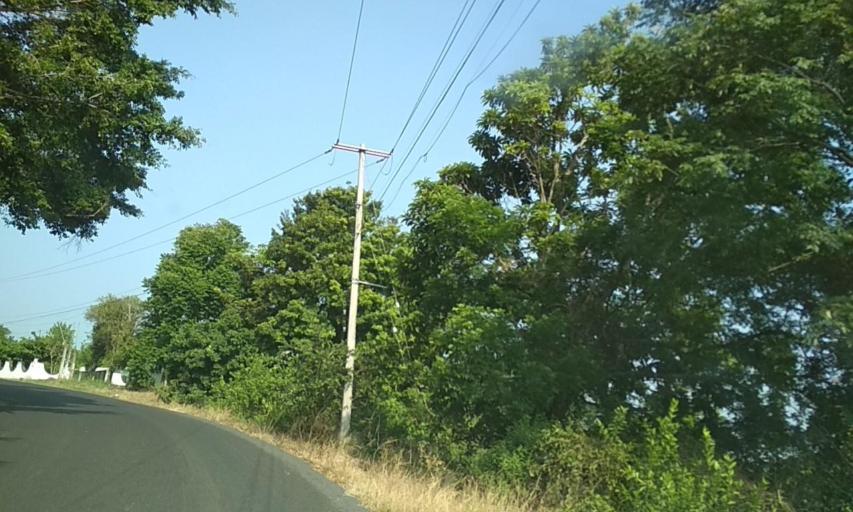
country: MX
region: Veracruz
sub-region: Misantla
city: La Defensa
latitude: 20.0505
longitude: -96.9838
